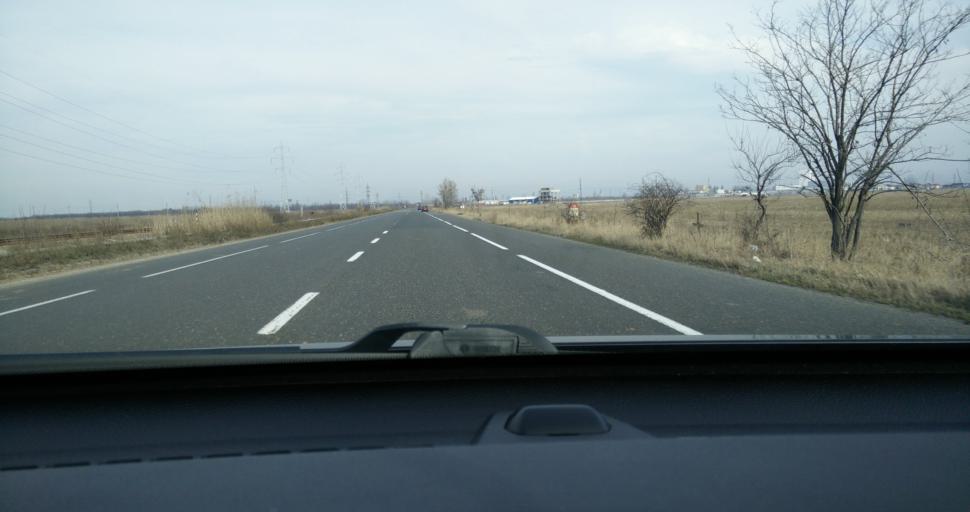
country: RO
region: Buzau
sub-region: Comuna Merei
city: Lipia
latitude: 45.1498
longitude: 26.7783
